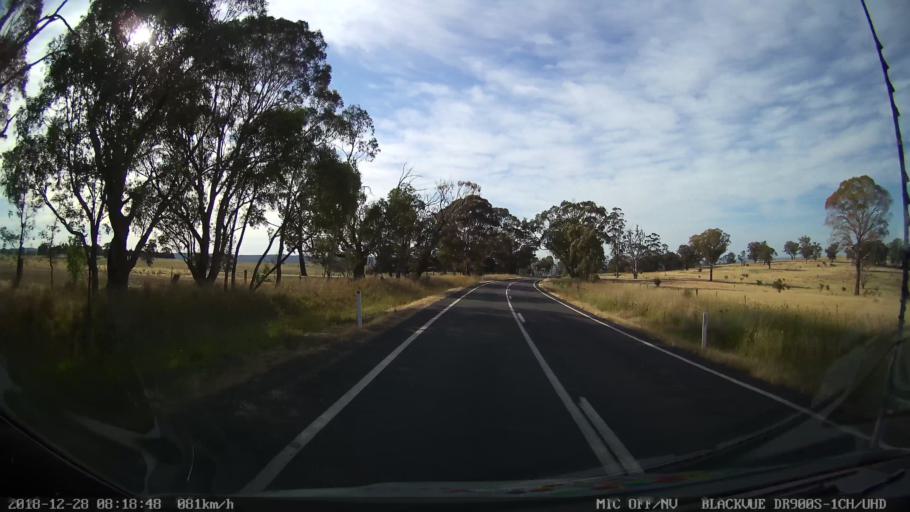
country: AU
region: New South Wales
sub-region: Blayney
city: Blayney
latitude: -33.8510
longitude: 149.3505
